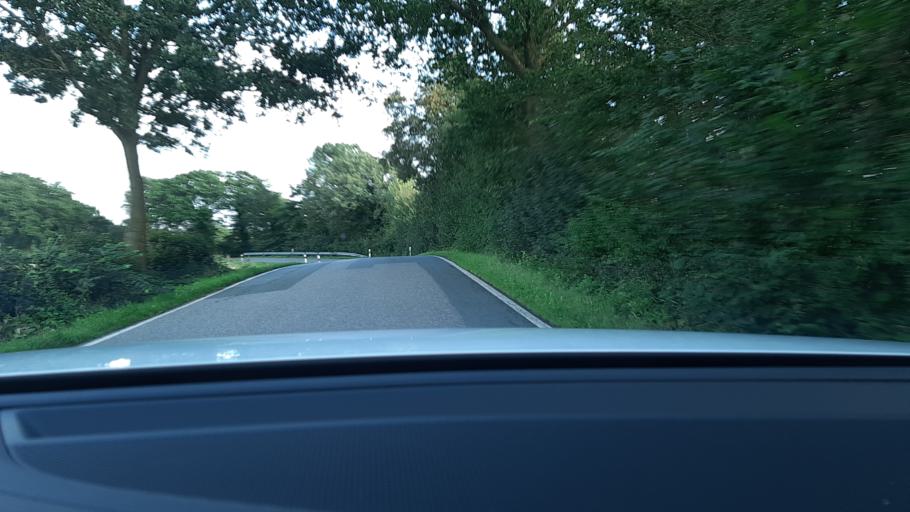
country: DE
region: Schleswig-Holstein
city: Stockelsdorf
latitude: 53.9198
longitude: 10.6197
